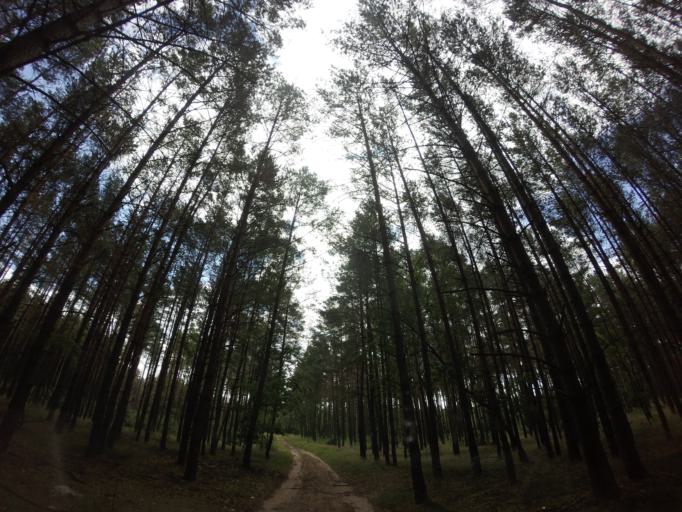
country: PL
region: Lubusz
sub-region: Powiat strzelecko-drezdenecki
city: Dobiegniew
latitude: 52.9952
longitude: 15.7238
